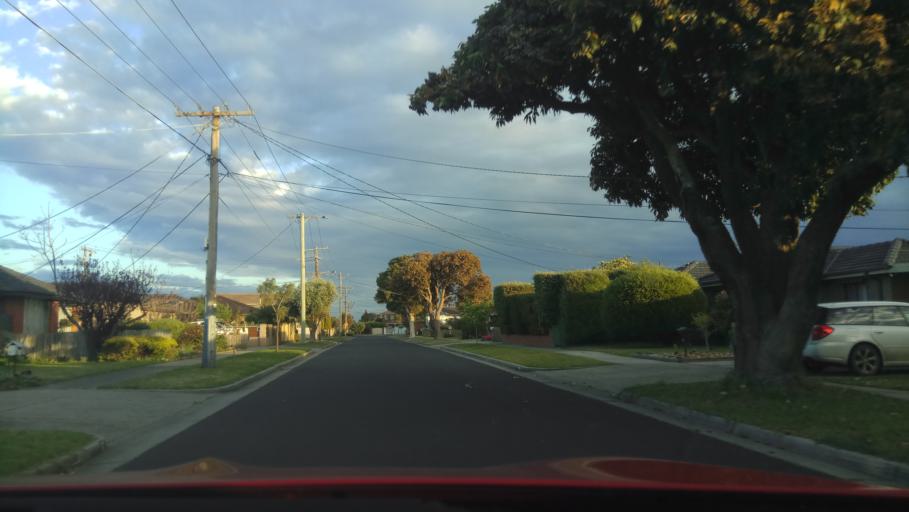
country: AU
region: Victoria
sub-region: Hobsons Bay
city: Seaholme
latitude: -37.8623
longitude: 144.8459
